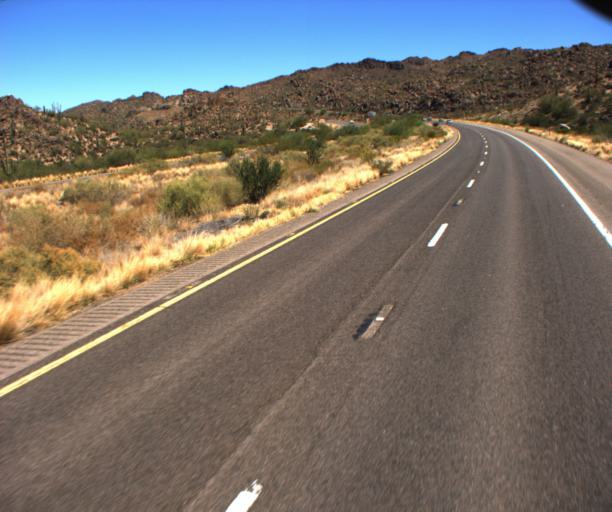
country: US
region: Arizona
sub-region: Maricopa County
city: Rio Verde
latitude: 33.6810
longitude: -111.5007
